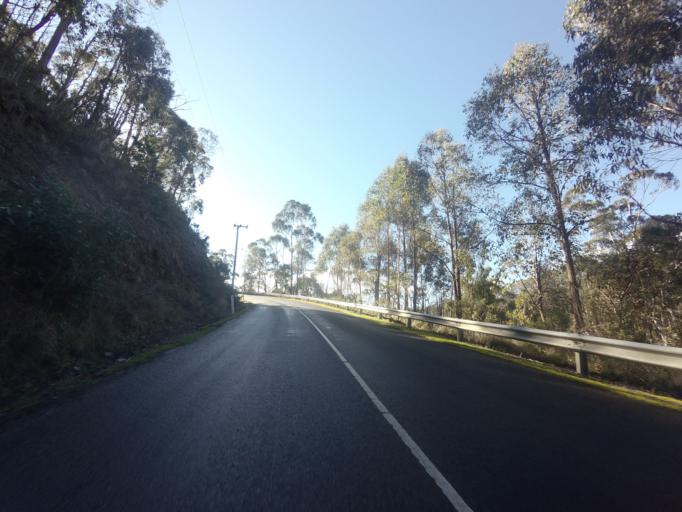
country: AU
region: Tasmania
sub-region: Glenorchy
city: Berriedale
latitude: -42.8252
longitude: 147.2070
